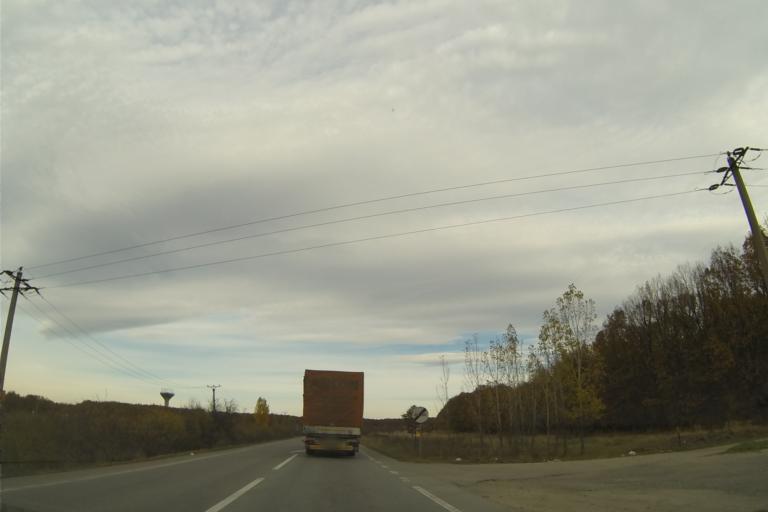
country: RO
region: Olt
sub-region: Comuna Scornicesti
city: Scornicesti
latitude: 44.5567
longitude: 24.5678
